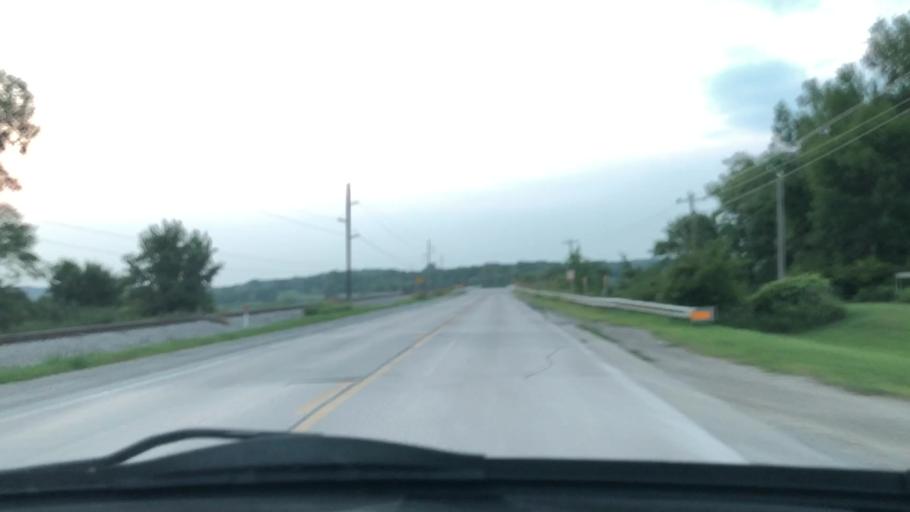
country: US
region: Iowa
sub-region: Johnson County
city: North Liberty
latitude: 41.8049
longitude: -91.6503
